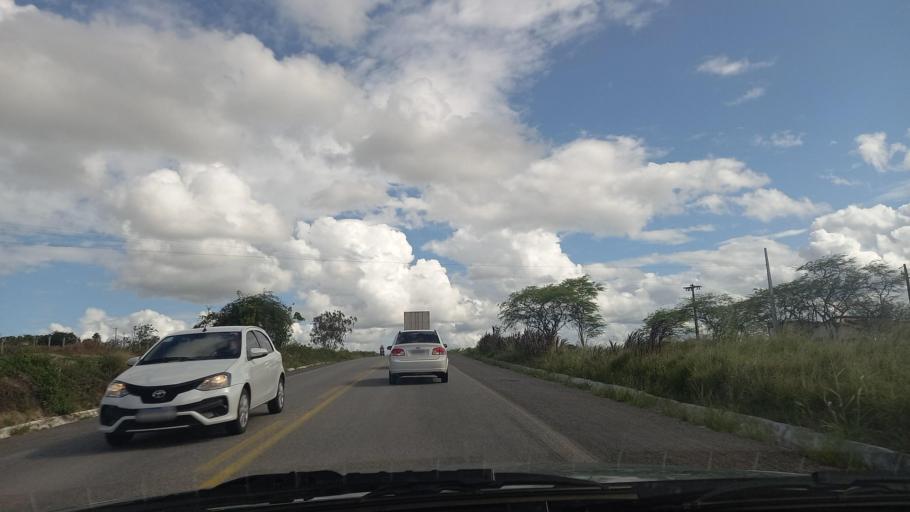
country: BR
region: Pernambuco
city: Garanhuns
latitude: -8.8010
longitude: -36.4395
